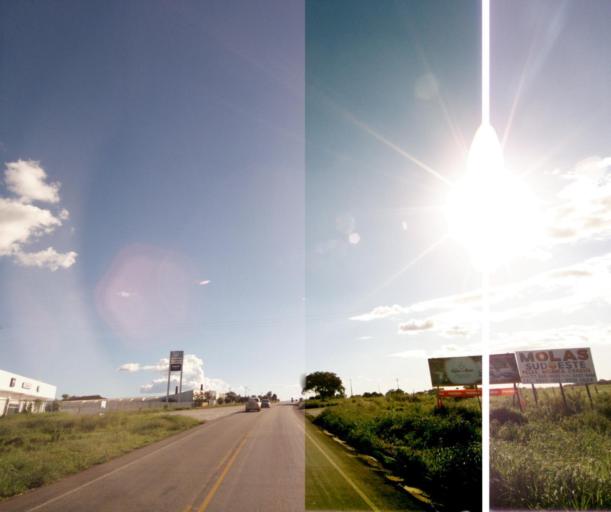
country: BR
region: Bahia
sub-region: Guanambi
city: Guanambi
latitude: -14.1891
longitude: -42.7419
